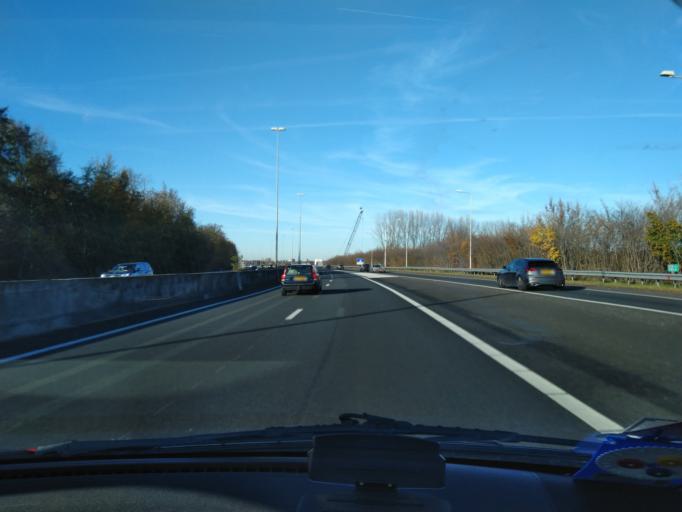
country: NL
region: Groningen
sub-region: Gemeente Haren
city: Haren
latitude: 53.1703
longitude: 6.5907
